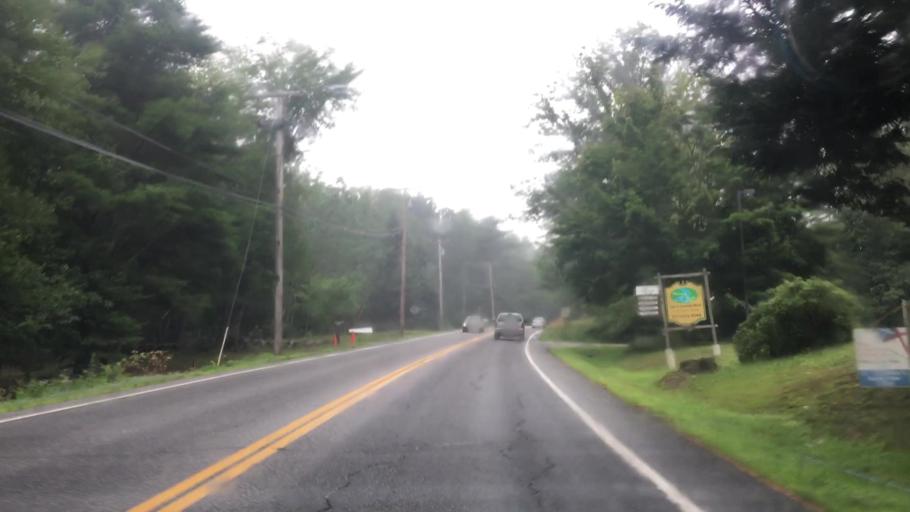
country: US
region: Maine
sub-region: Lincoln County
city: Boothbay
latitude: 43.9139
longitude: -69.6148
